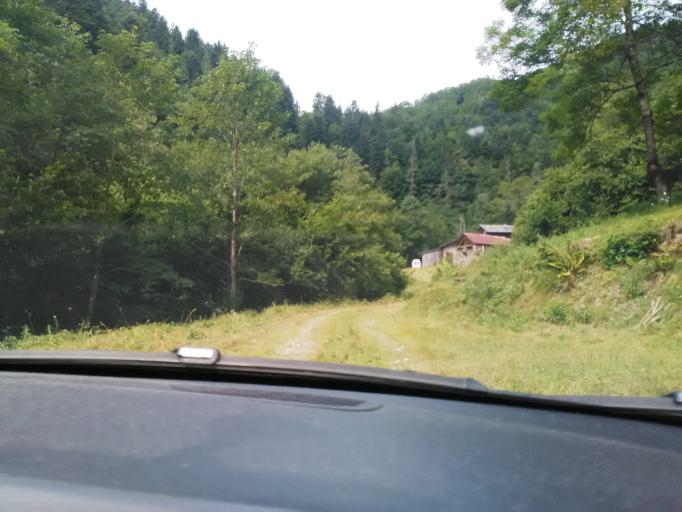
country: IT
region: Piedmont
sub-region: Provincia di Vercelli
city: Cervatto
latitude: 45.8784
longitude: 8.1548
